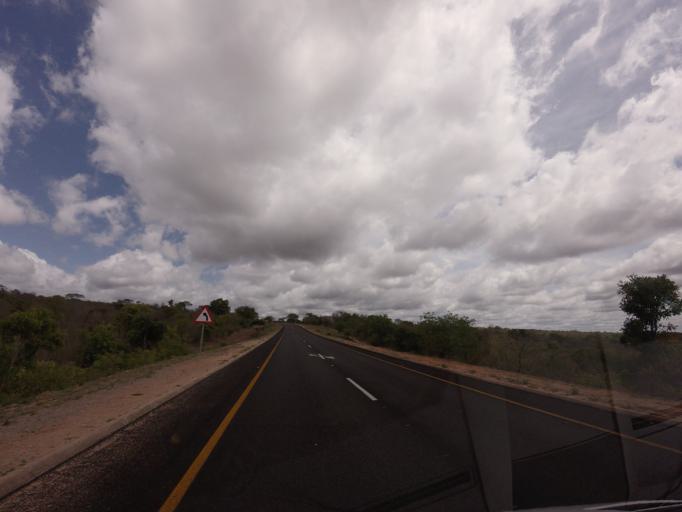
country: ZA
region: Limpopo
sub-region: Mopani District Municipality
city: Hoedspruit
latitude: -24.5582
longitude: 31.0443
